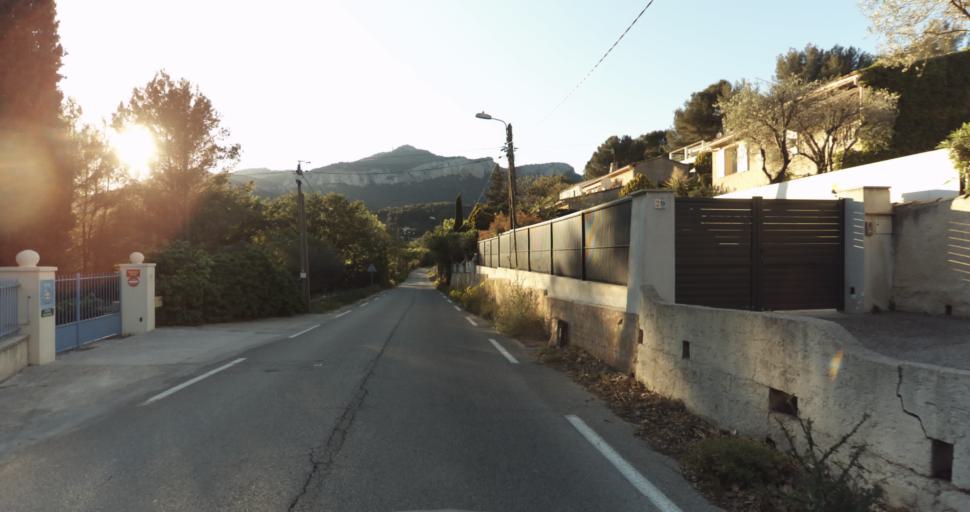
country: FR
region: Provence-Alpes-Cote d'Azur
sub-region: Departement du Var
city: Le Revest-les-Eaux
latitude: 43.1674
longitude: 5.9367
